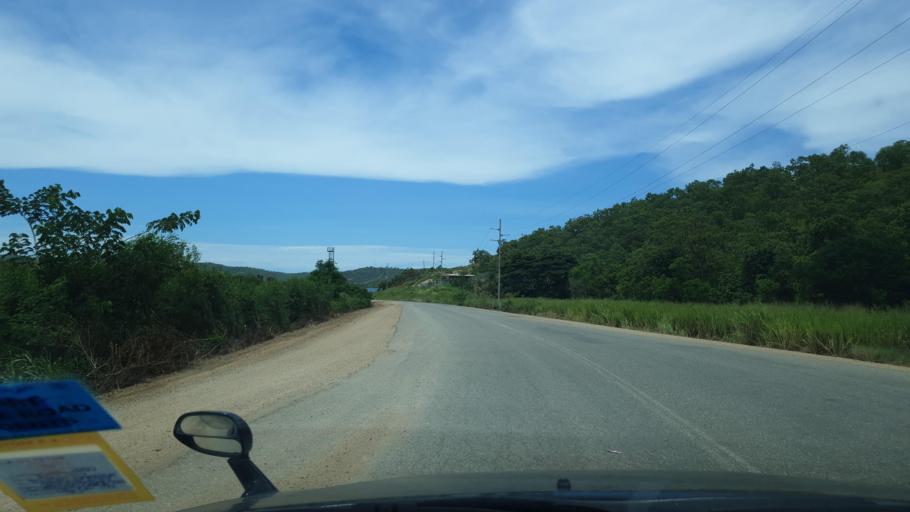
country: PG
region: National Capital
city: Port Moresby
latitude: -9.4156
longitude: 147.1002
